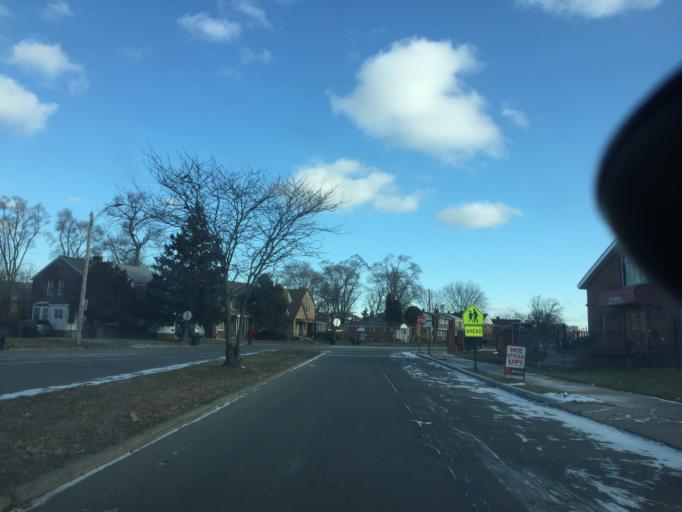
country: US
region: Michigan
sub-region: Wayne County
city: Highland Park
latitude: 42.3962
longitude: -83.1289
